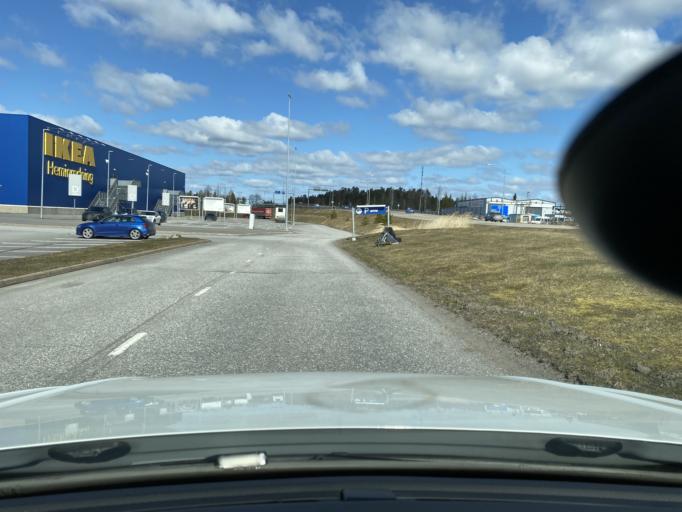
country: FI
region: Varsinais-Suomi
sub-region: Turku
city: Rusko
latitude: 60.4938
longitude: 22.2305
